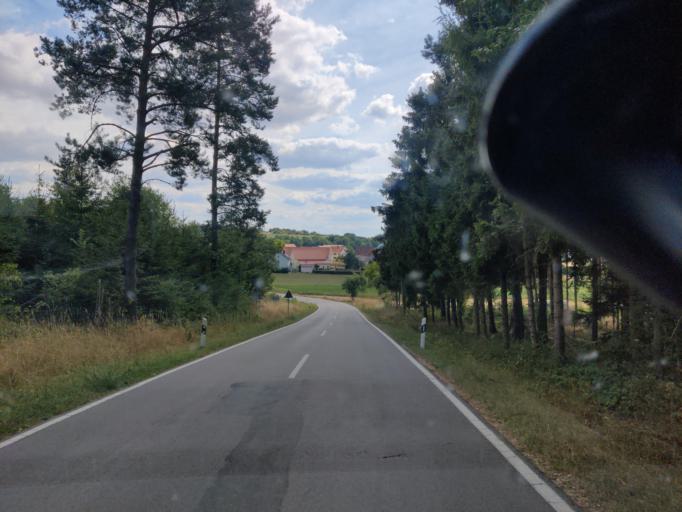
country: DE
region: Bavaria
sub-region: Regierungsbezirk Mittelfranken
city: Bergen
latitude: 49.0804
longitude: 11.1542
